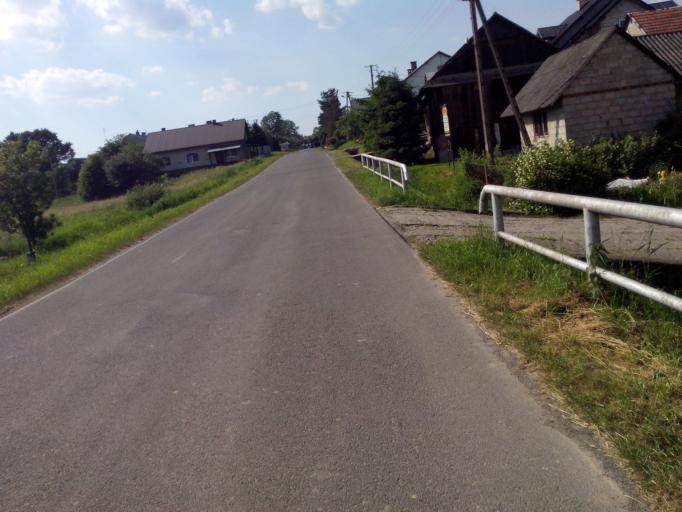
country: PL
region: Subcarpathian Voivodeship
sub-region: Powiat brzozowski
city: Stara Wies
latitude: 49.7288
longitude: 21.9890
